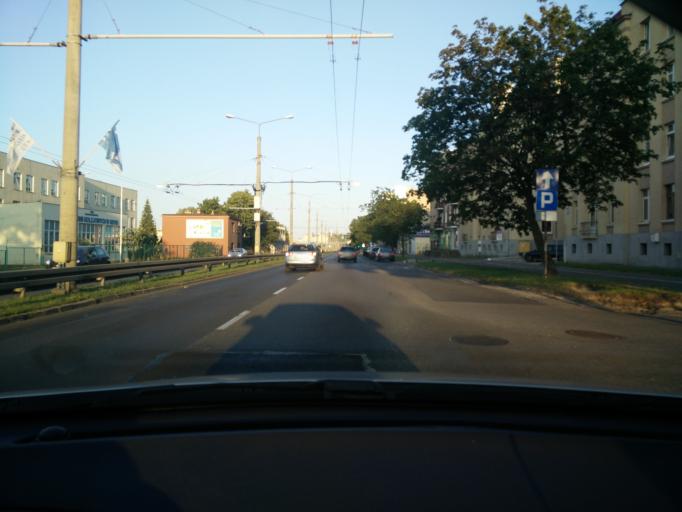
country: PL
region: Pomeranian Voivodeship
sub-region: Gdynia
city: Gdynia
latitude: 54.5240
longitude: 18.5190
